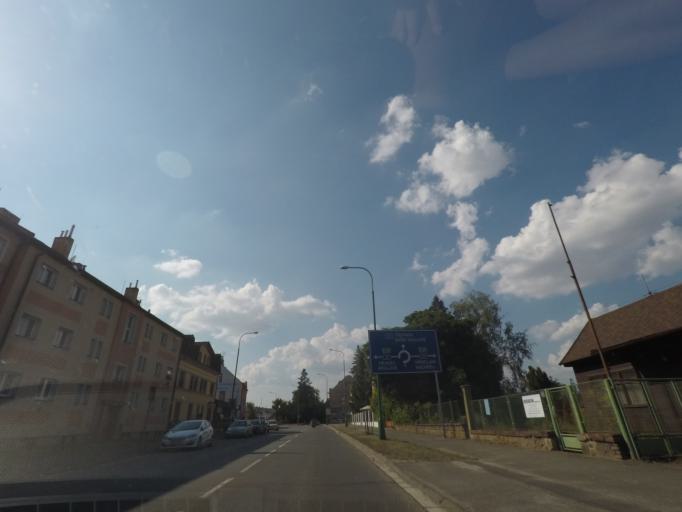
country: CZ
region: Kralovehradecky
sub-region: Okres Nachod
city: Jaromer
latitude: 50.3478
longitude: 15.9146
